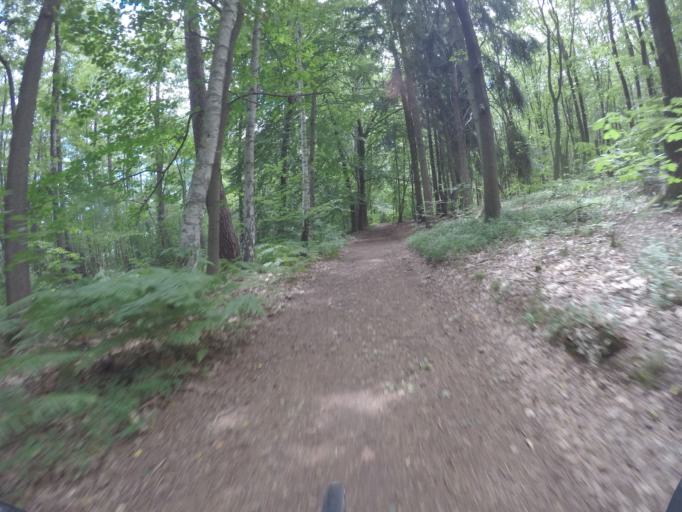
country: DE
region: Brandenburg
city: Reichenwalde
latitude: 52.2277
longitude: 13.9818
